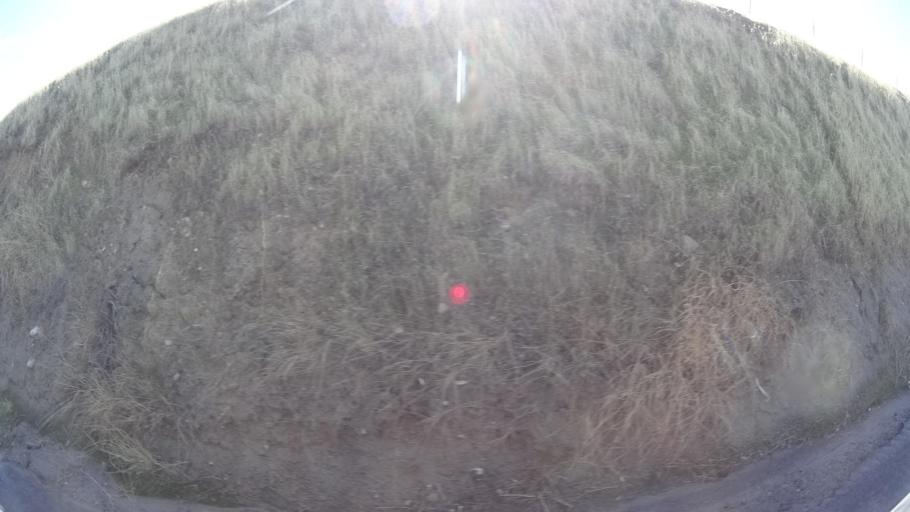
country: US
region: California
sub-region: Kern County
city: Lamont
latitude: 35.3978
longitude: -118.8126
